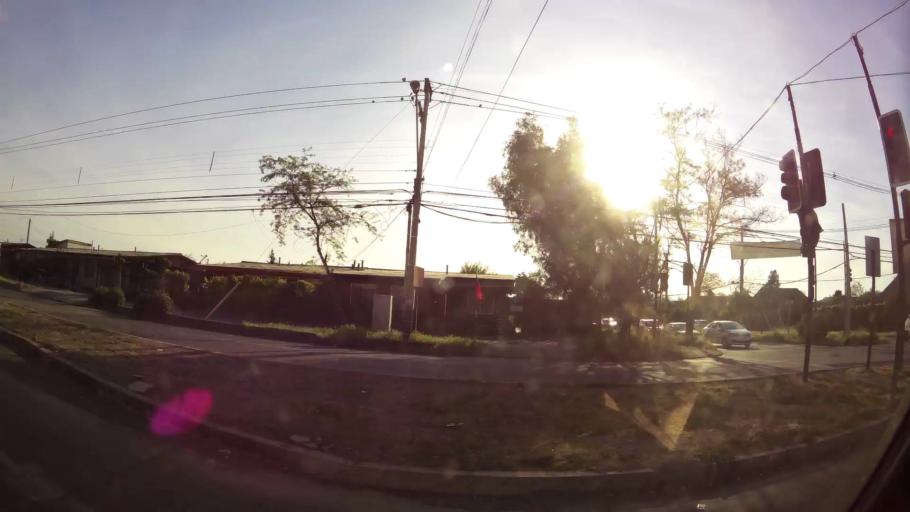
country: CL
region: Santiago Metropolitan
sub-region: Provincia de Santiago
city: Villa Presidente Frei, Nunoa, Santiago, Chile
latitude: -33.5132
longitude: -70.6111
